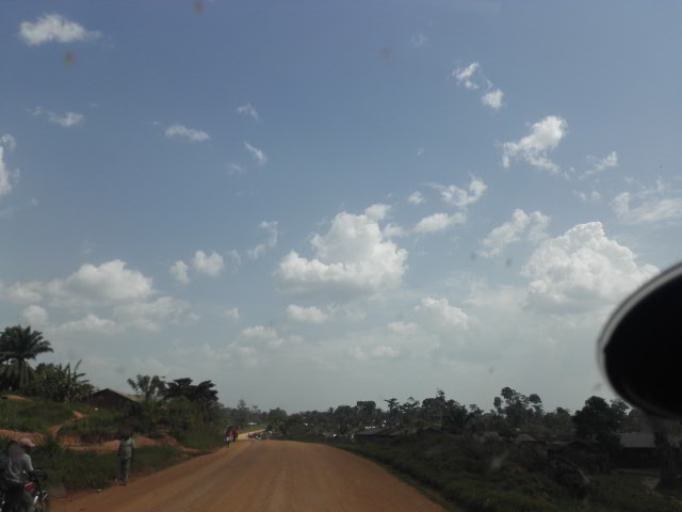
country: CD
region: Nord Kivu
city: Beni
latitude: 1.0631
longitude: 29.5836
